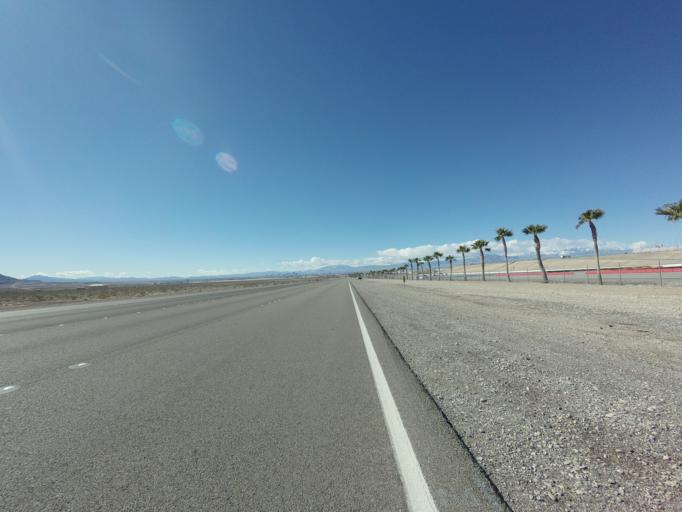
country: US
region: Nevada
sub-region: Clark County
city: Nellis Air Force Base
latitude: 36.2700
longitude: -115.0039
